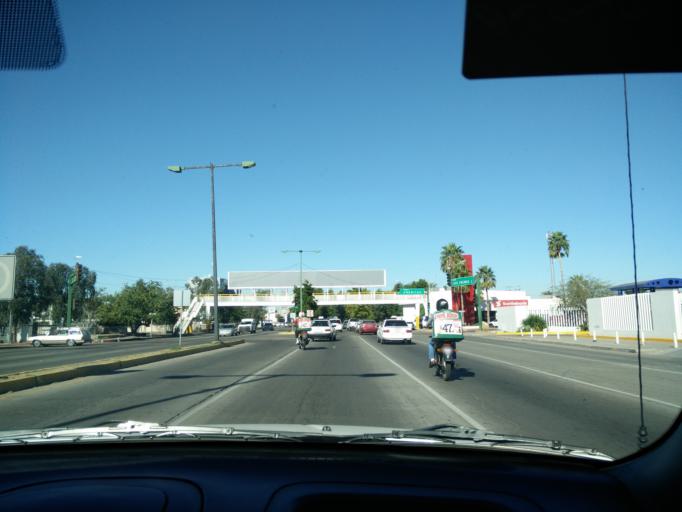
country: MX
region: Sonora
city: Hermosillo
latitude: 29.0907
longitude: -110.9716
